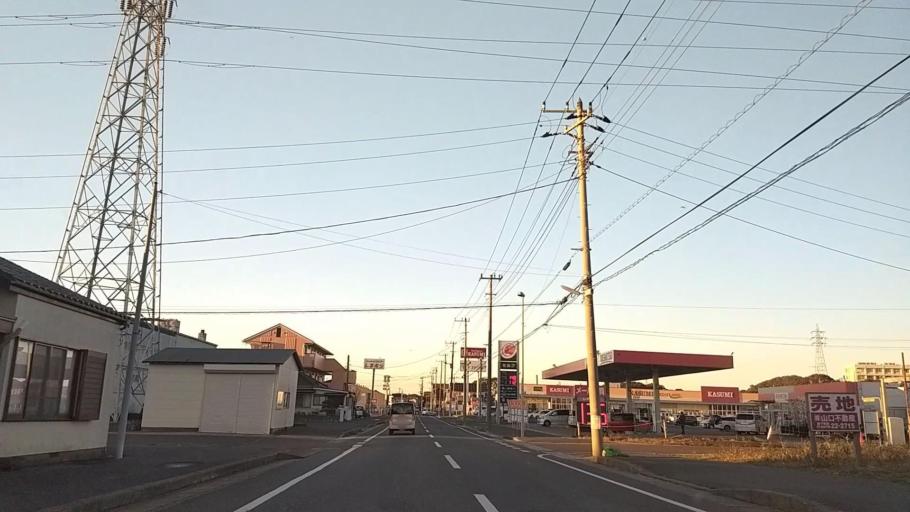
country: JP
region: Chiba
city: Hasaki
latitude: 35.7190
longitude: 140.8364
